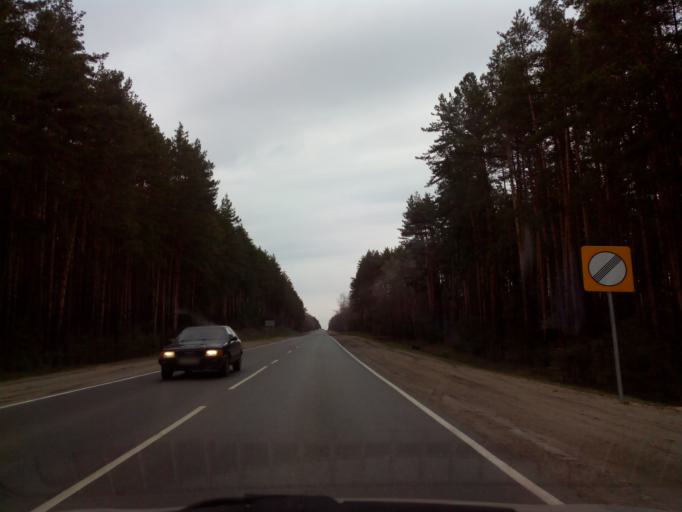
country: RU
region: Tambov
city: Znamenka
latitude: 52.5380
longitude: 41.3553
